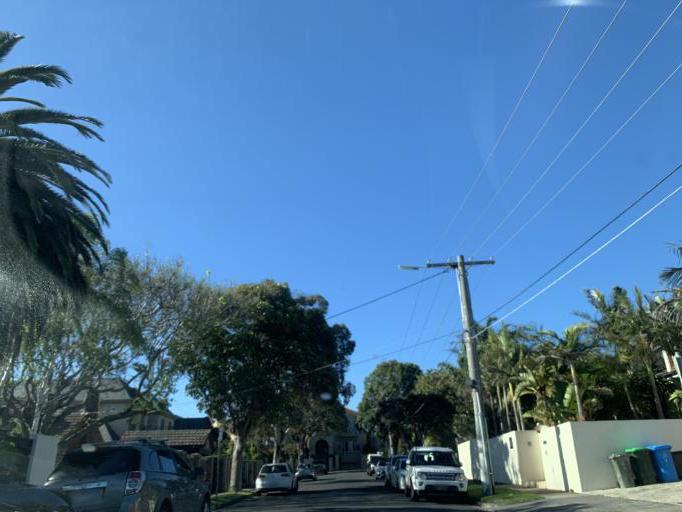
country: AU
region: Victoria
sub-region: Bayside
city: Hampton
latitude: -37.9273
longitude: 144.9915
